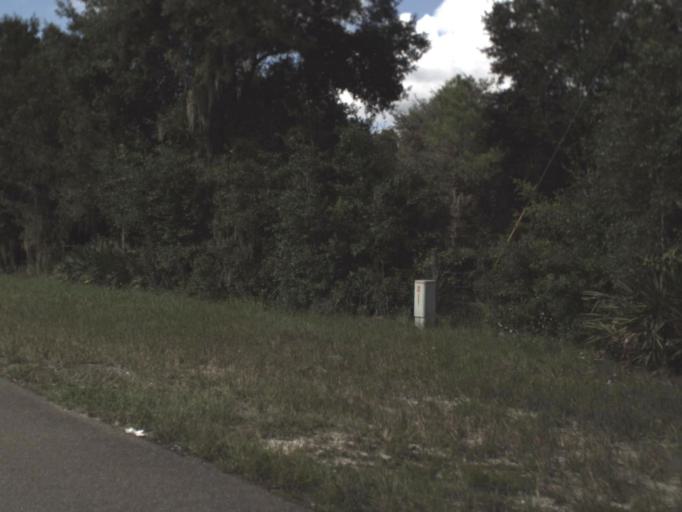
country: US
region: Florida
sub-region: Hardee County
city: Wauchula
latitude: 27.4869
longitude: -82.0159
